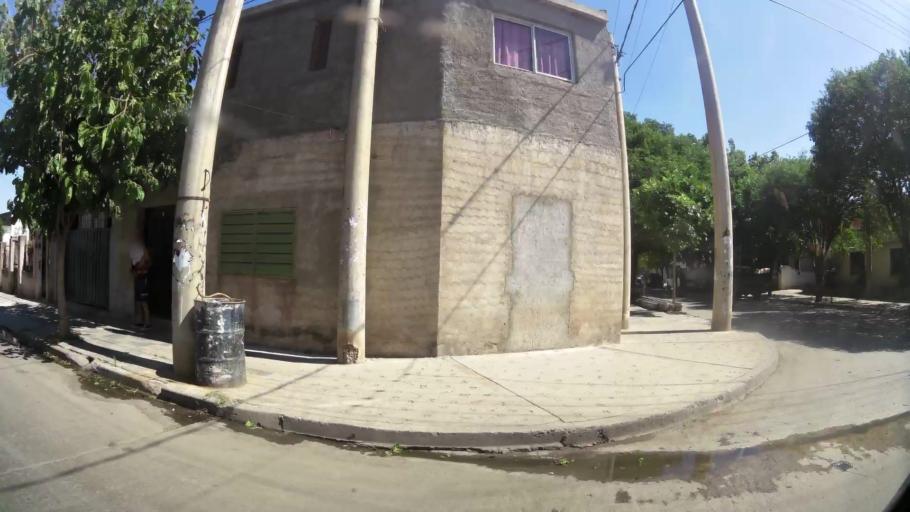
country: AR
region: Cordoba
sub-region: Departamento de Capital
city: Cordoba
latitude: -31.3739
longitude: -64.1541
